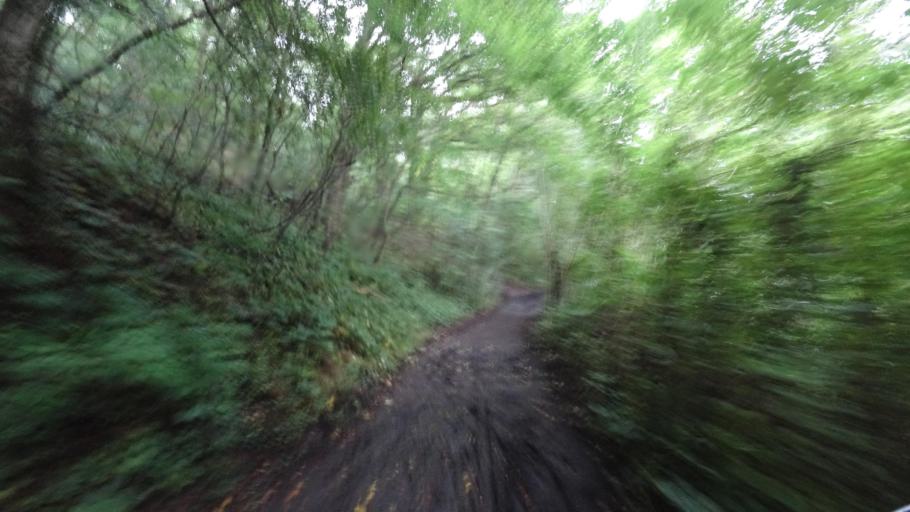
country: BE
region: Wallonia
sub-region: Province du Brabant Wallon
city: Mont-Saint-Guibert
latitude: 50.6325
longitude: 4.6322
